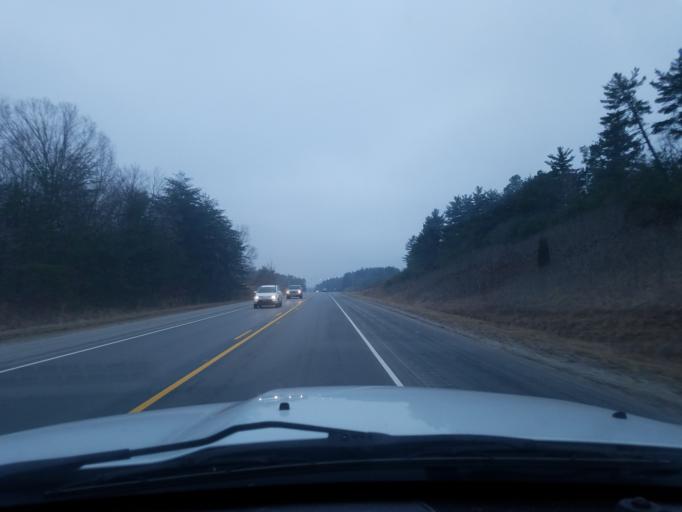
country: US
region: Indiana
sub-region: Perry County
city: Tell City
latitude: 38.1122
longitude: -86.6096
